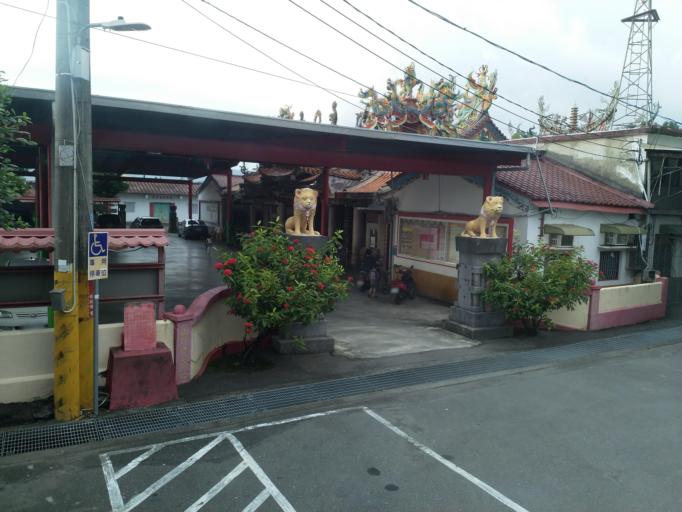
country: TW
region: Taiwan
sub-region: Pingtung
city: Pingtung
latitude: 22.8663
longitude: 120.5436
